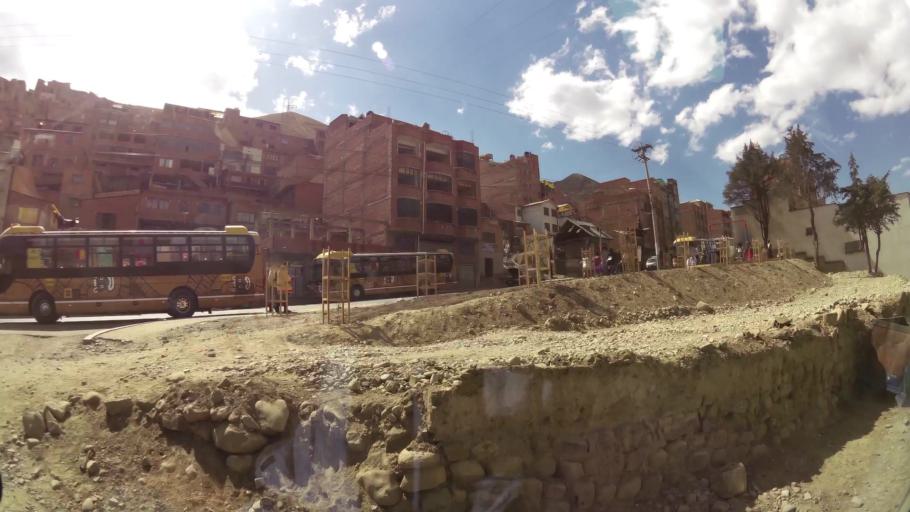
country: BO
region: La Paz
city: La Paz
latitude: -16.4622
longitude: -68.1066
